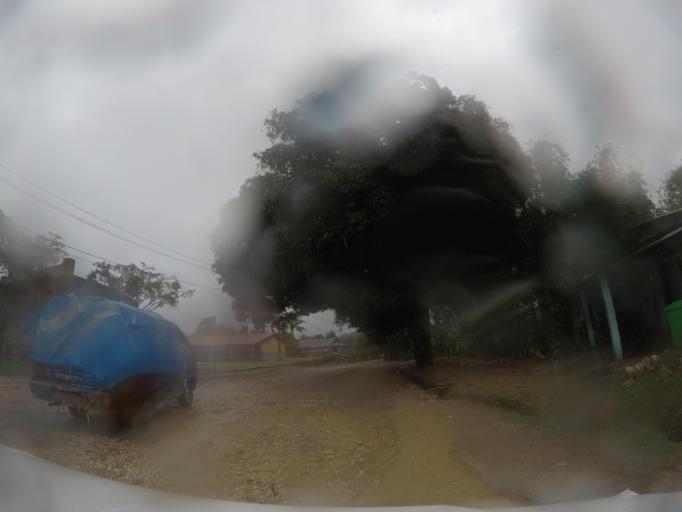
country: TL
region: Baucau
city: Venilale
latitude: -8.6438
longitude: 126.3783
